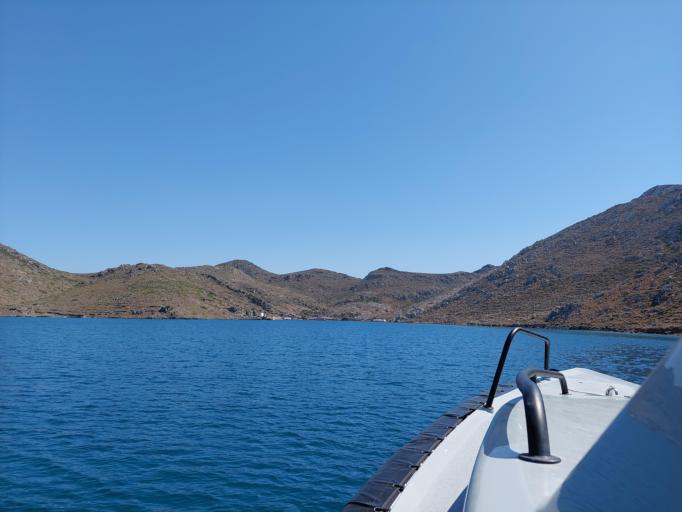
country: GR
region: South Aegean
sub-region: Nomos Dodekanisou
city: Karpathos
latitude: 35.8211
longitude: 27.2140
